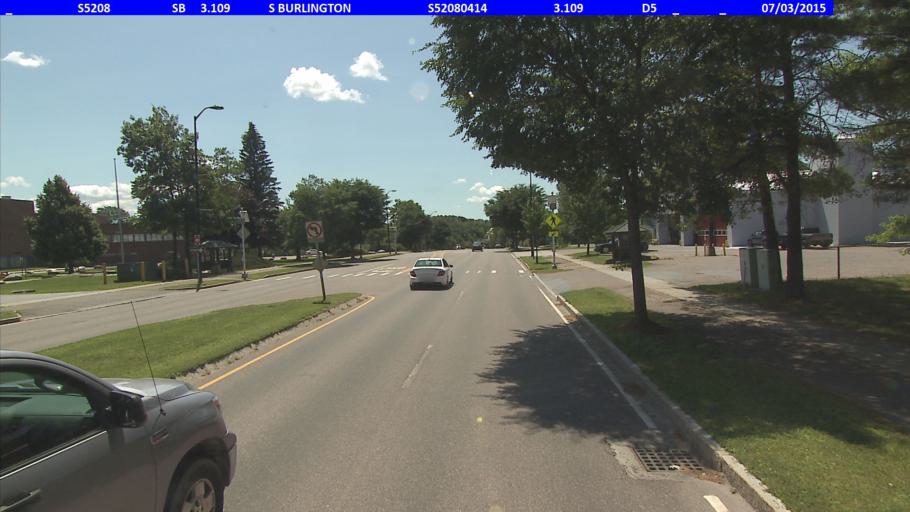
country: US
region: Vermont
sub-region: Chittenden County
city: South Burlington
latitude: 44.4551
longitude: -73.1792
